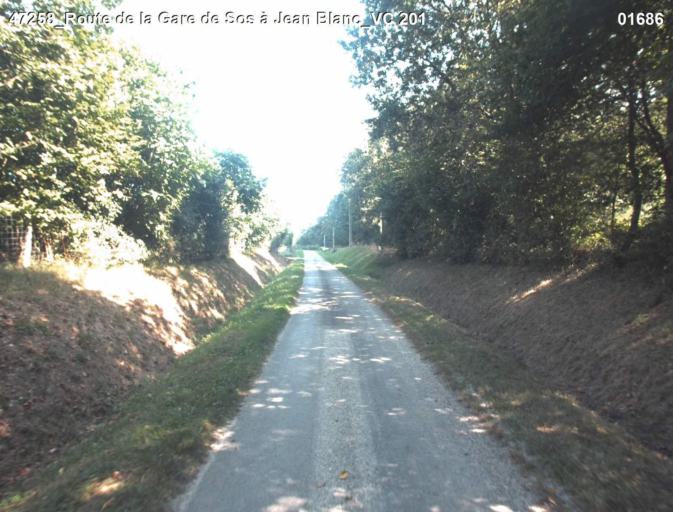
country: FR
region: Midi-Pyrenees
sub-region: Departement du Gers
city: Montreal
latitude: 44.0324
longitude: 0.1555
